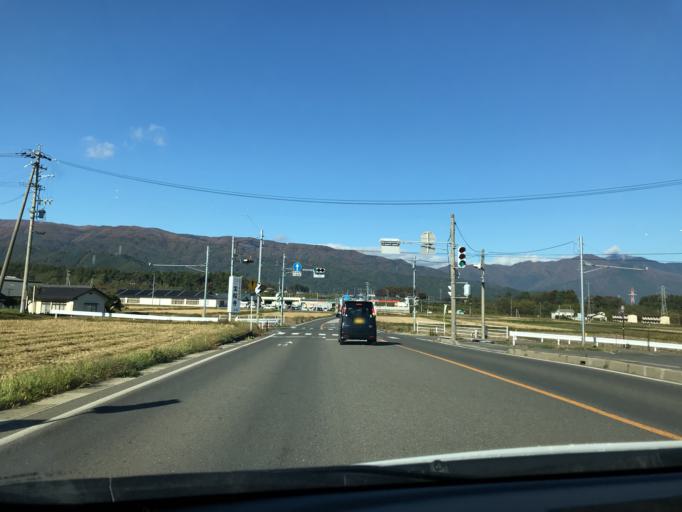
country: JP
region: Nagano
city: Shiojiri
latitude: 36.1483
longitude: 137.9063
